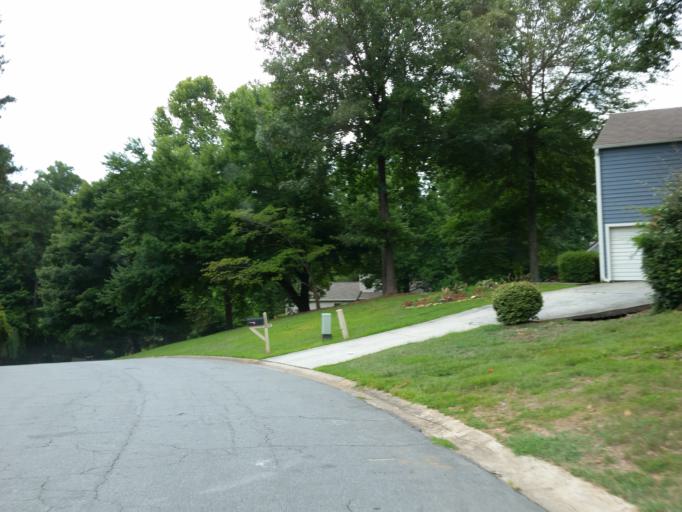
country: US
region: Georgia
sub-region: Cobb County
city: Marietta
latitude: 34.0008
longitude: -84.4753
